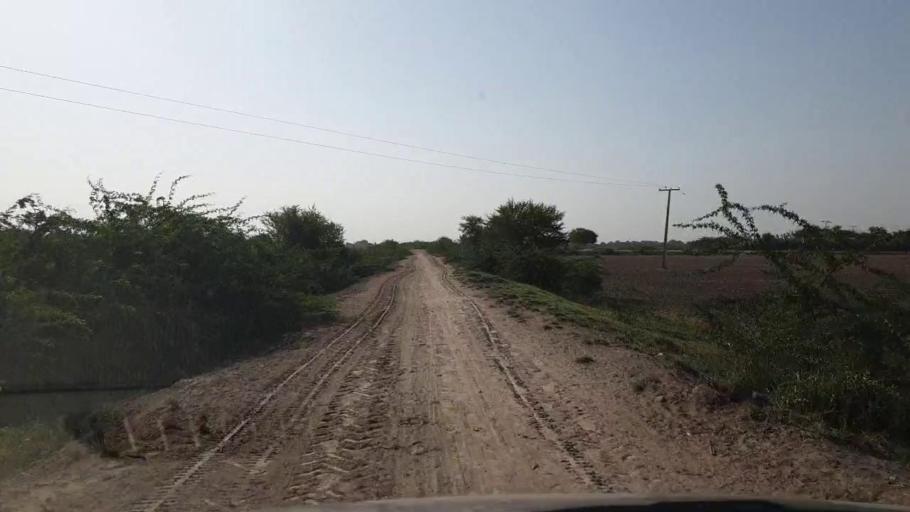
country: PK
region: Sindh
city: Kadhan
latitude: 24.5943
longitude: 69.0758
